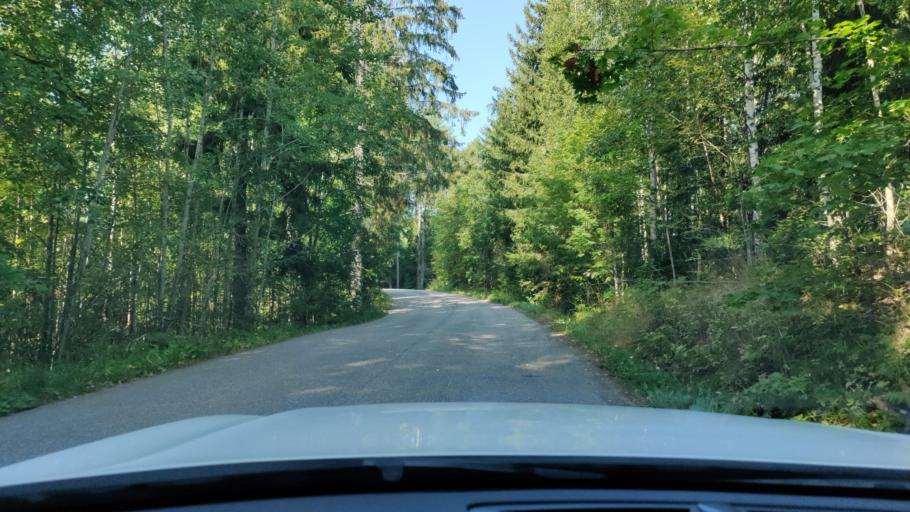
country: FI
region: Haeme
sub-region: Haemeenlinna
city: Tervakoski
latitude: 60.6734
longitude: 24.6371
